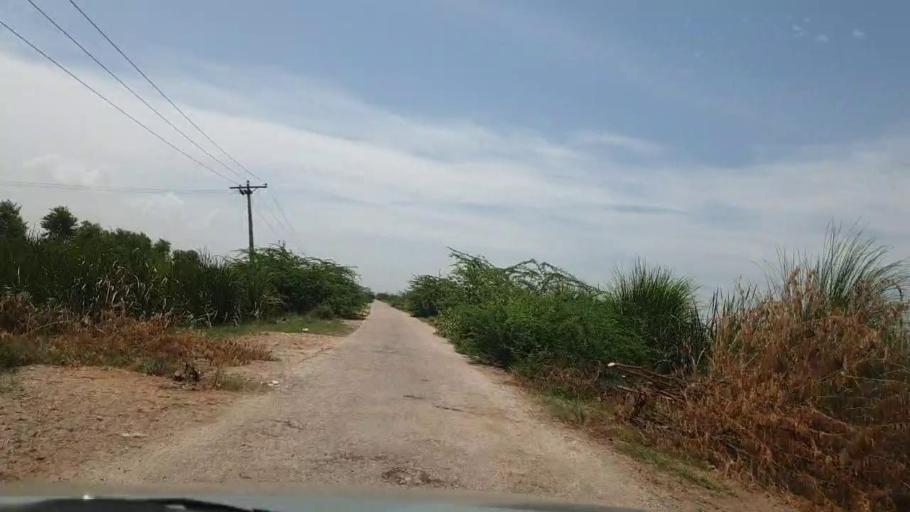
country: PK
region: Sindh
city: Bozdar
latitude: 27.0655
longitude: 68.9826
